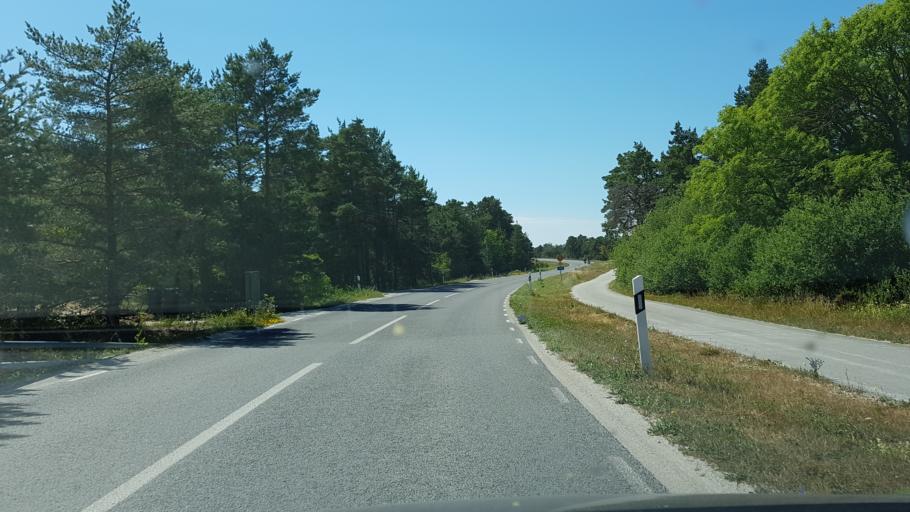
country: SE
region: Gotland
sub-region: Gotland
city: Visby
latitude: 57.6943
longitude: 18.3755
